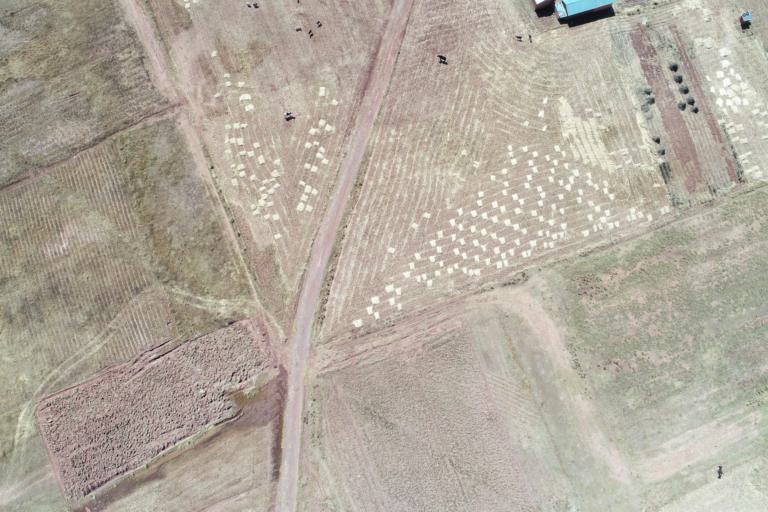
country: BO
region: La Paz
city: Tiahuanaco
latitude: -16.5895
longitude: -68.7707
